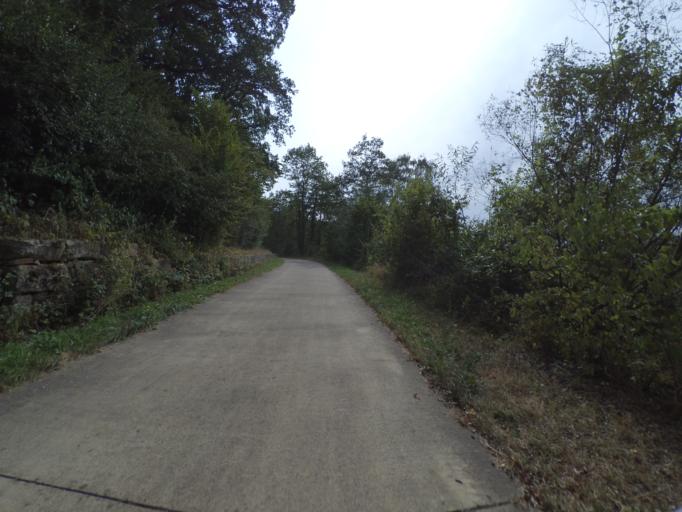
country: LU
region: Grevenmacher
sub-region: Canton de Remich
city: Bous
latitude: 49.5324
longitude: 6.3287
